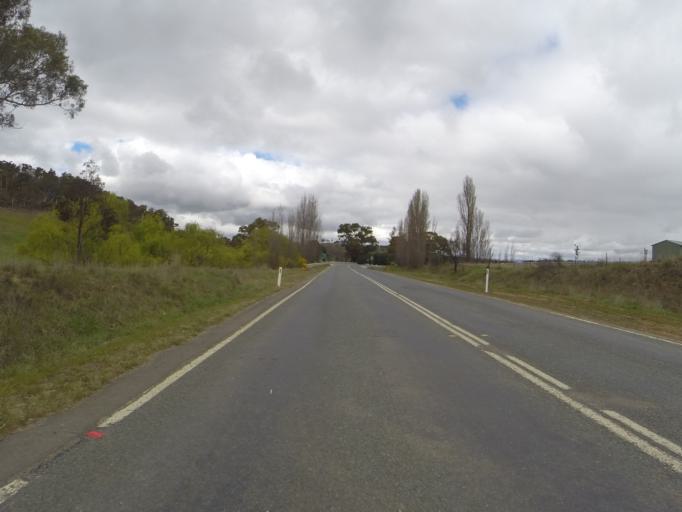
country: AU
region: Australian Capital Territory
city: Canberra
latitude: -35.2322
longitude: 149.1976
